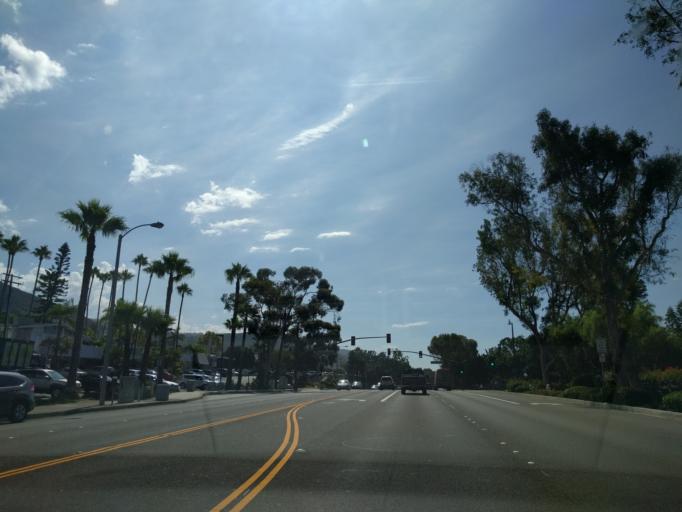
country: US
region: California
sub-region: Orange County
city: Laguna Beach
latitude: 33.5168
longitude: -117.7579
